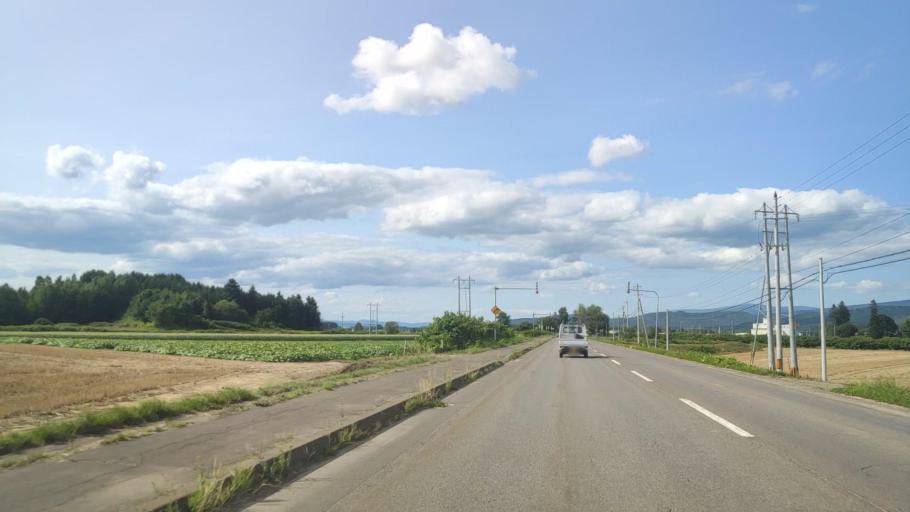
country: JP
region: Hokkaido
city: Nayoro
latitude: 44.4252
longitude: 142.4004
